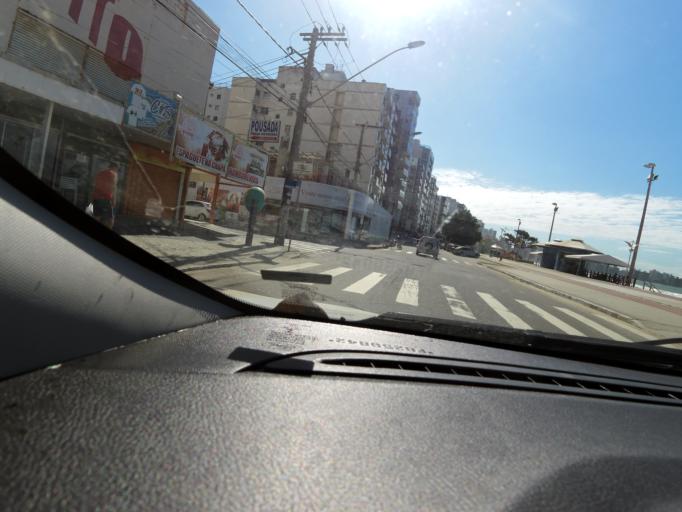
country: BR
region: Espirito Santo
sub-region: Guarapari
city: Guarapari
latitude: -20.6563
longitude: -40.4910
